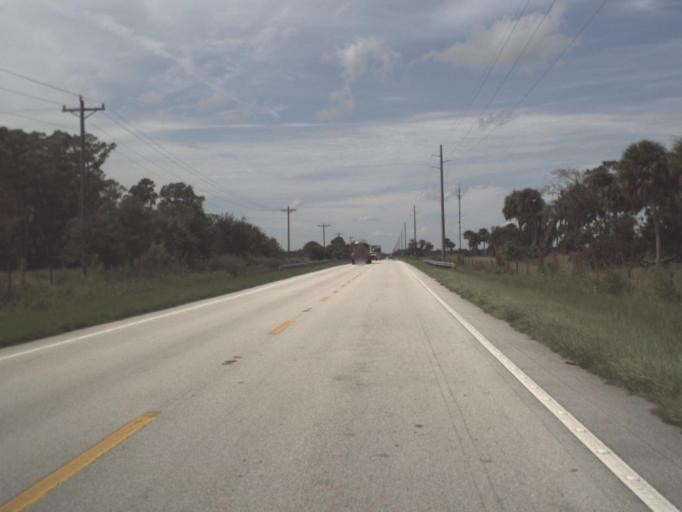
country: US
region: Florida
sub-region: Highlands County
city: Placid Lakes
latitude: 27.2089
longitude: -81.4232
